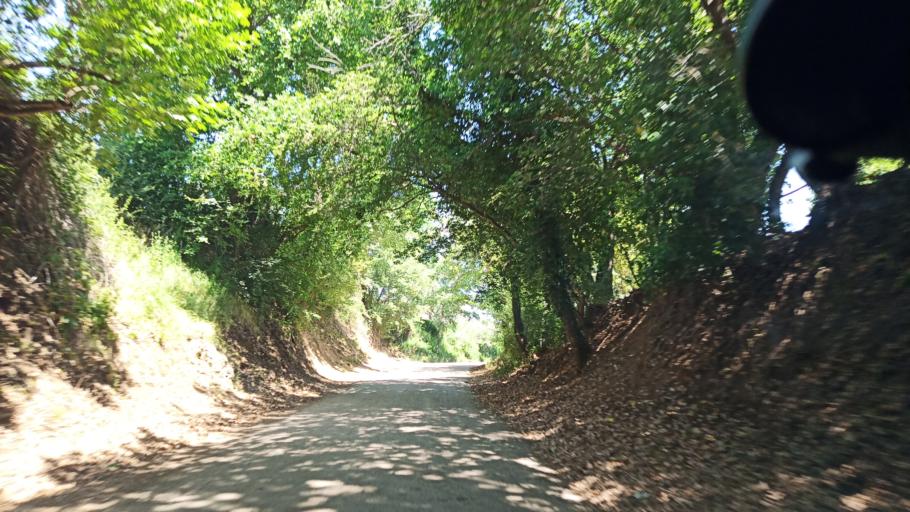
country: IT
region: Latium
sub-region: Provincia di Rieti
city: Torri in Sabina
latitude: 42.3465
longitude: 12.6183
